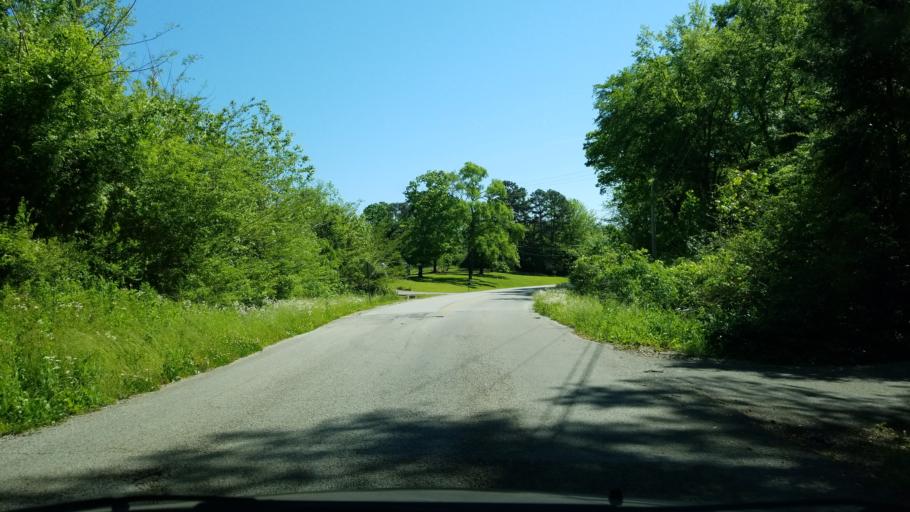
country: US
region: Tennessee
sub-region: Hamilton County
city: Walden
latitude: 35.1575
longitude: -85.2886
